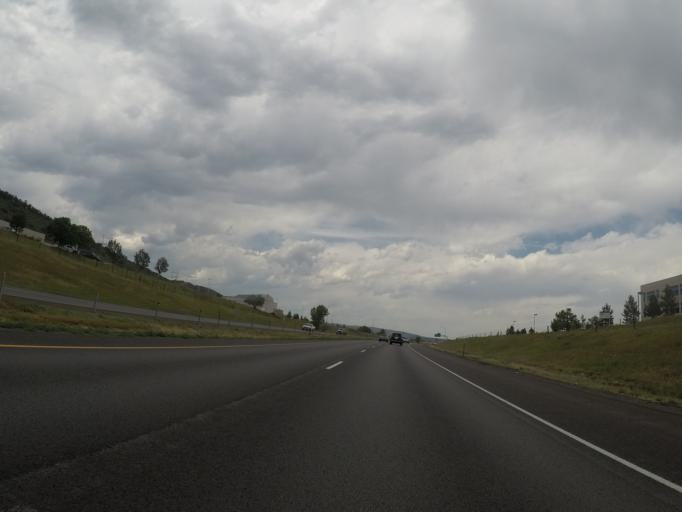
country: US
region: Colorado
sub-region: Jefferson County
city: Ken Caryl
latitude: 39.6037
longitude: -105.1537
